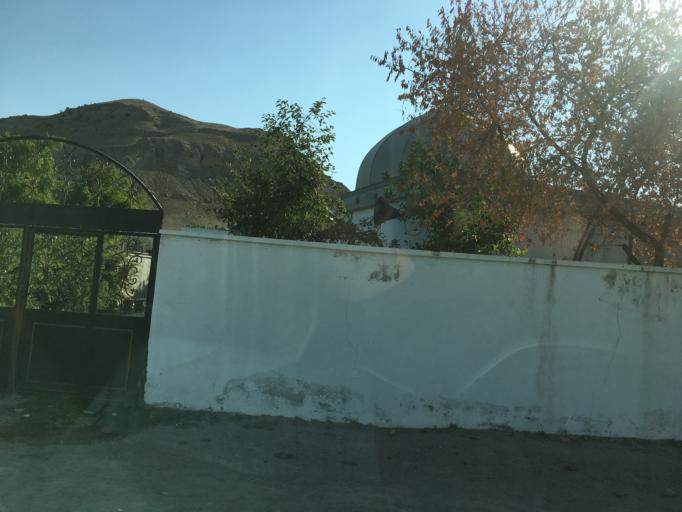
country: TM
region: Balkan
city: Magtymguly
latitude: 38.3016
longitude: 56.7446
